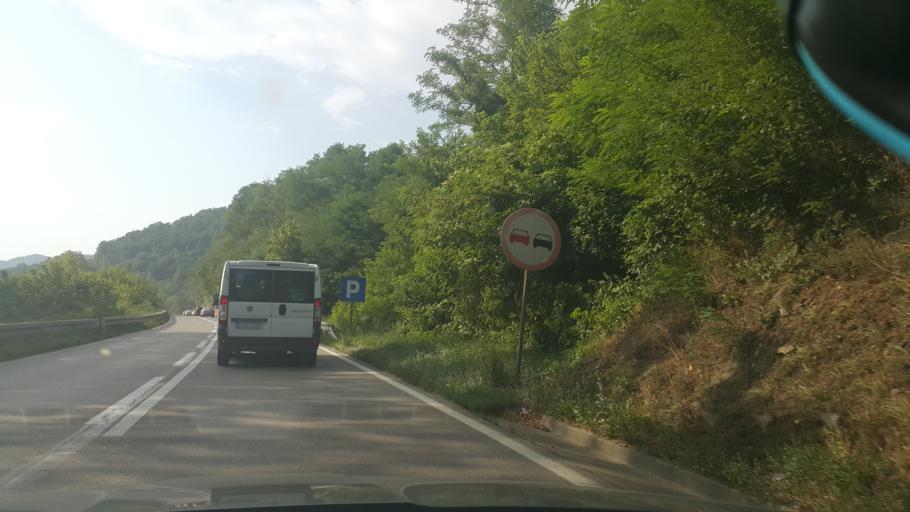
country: RS
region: Central Serbia
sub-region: Jablanicki Okrug
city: Vlasotince
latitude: 42.8500
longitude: 22.1321
